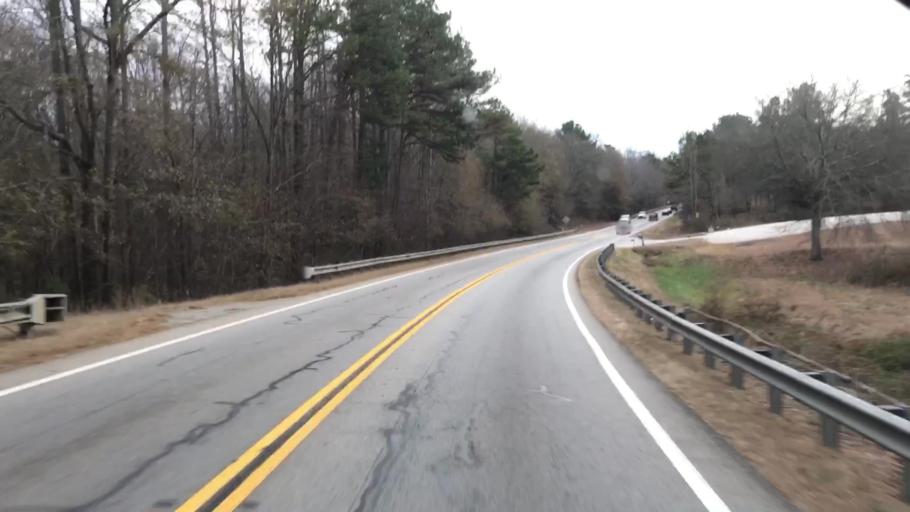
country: US
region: Georgia
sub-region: Jackson County
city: Hoschton
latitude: 34.0571
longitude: -83.7803
